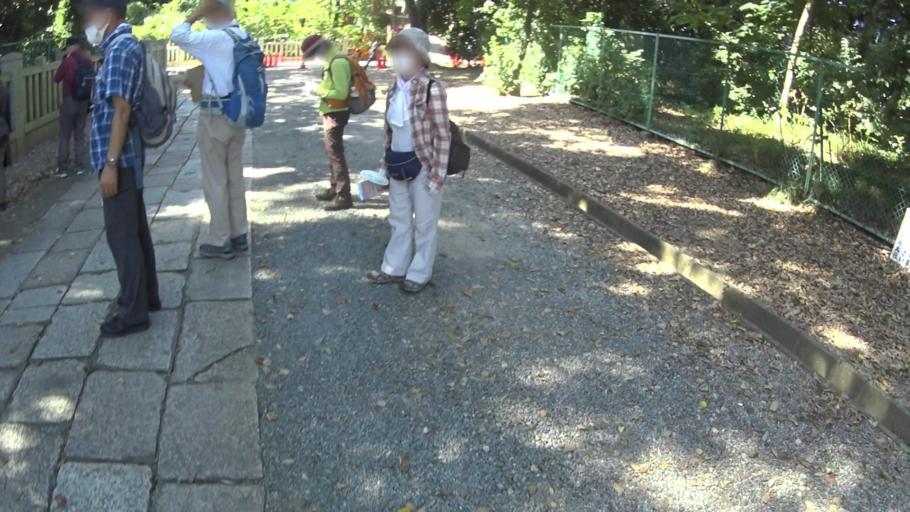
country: JP
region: Osaka
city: Sakai
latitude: 34.5347
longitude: 135.4913
